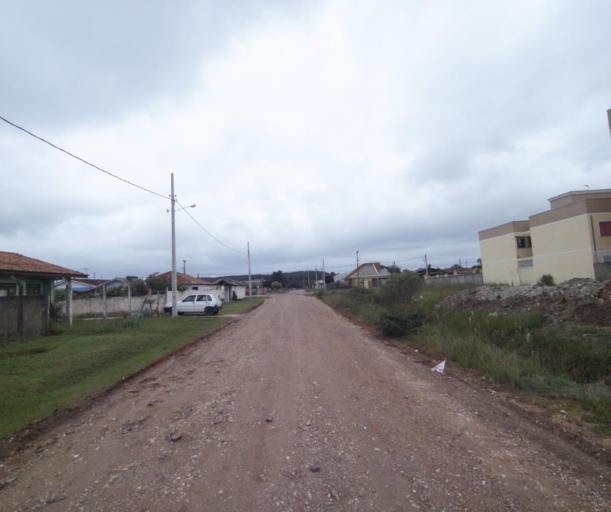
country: BR
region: Parana
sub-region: Quatro Barras
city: Quatro Barras
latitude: -25.3602
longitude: -49.0954
